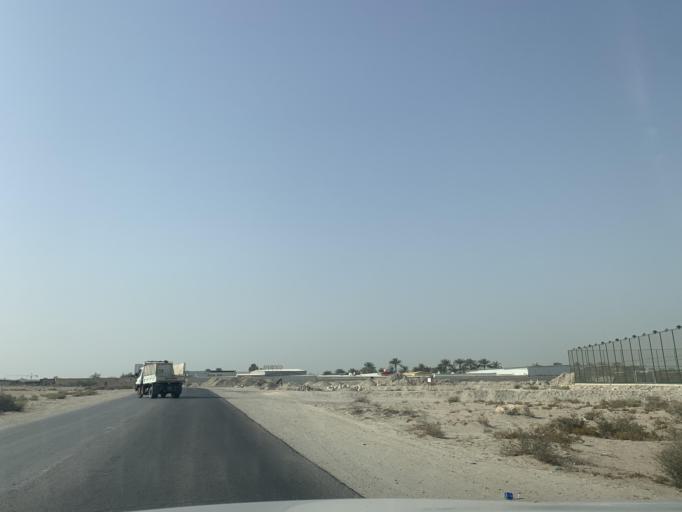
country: BH
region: Central Governorate
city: Madinat Hamad
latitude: 26.1603
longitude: 50.4884
